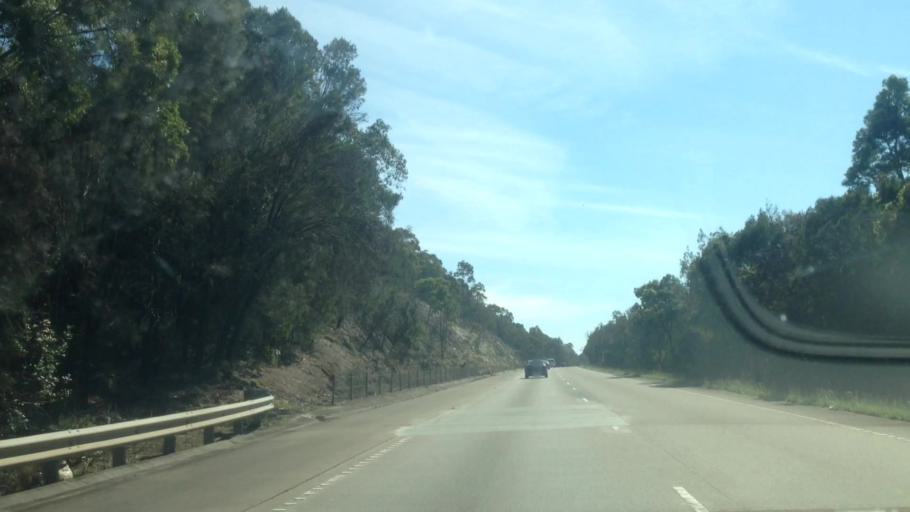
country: AU
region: New South Wales
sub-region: Lake Macquarie Shire
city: Fennell Bay
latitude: -32.9636
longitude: 151.5381
